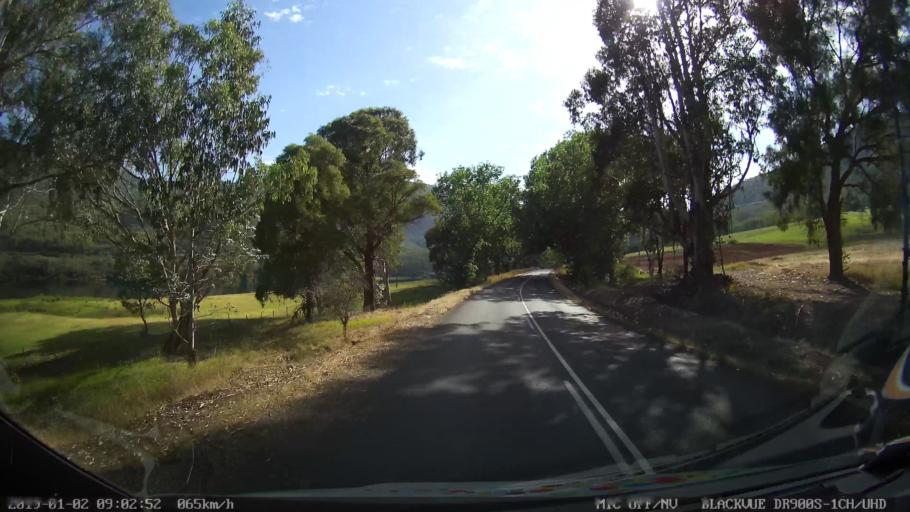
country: AU
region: New South Wales
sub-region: Tumut Shire
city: Tumut
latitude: -35.5701
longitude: 148.3166
